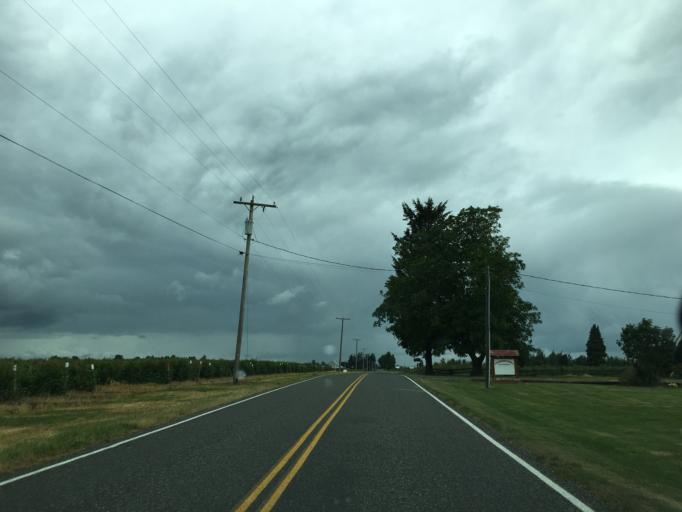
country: US
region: Washington
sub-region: Whatcom County
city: Everson
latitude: 48.9819
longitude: -122.3538
